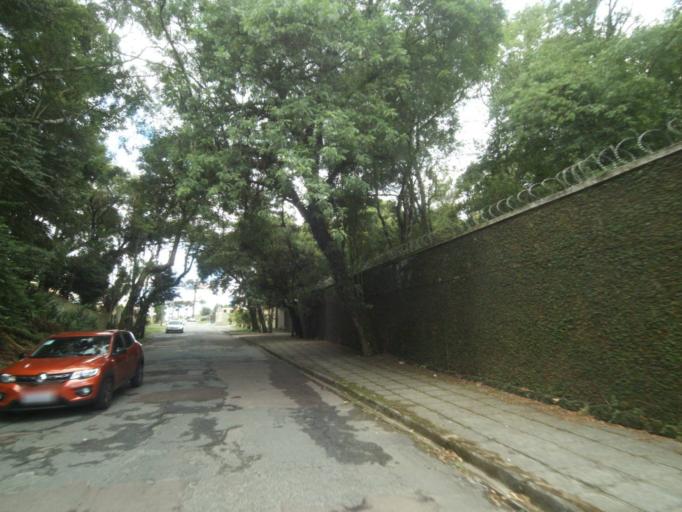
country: BR
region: Parana
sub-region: Curitiba
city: Curitiba
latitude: -25.4348
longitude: -49.3397
